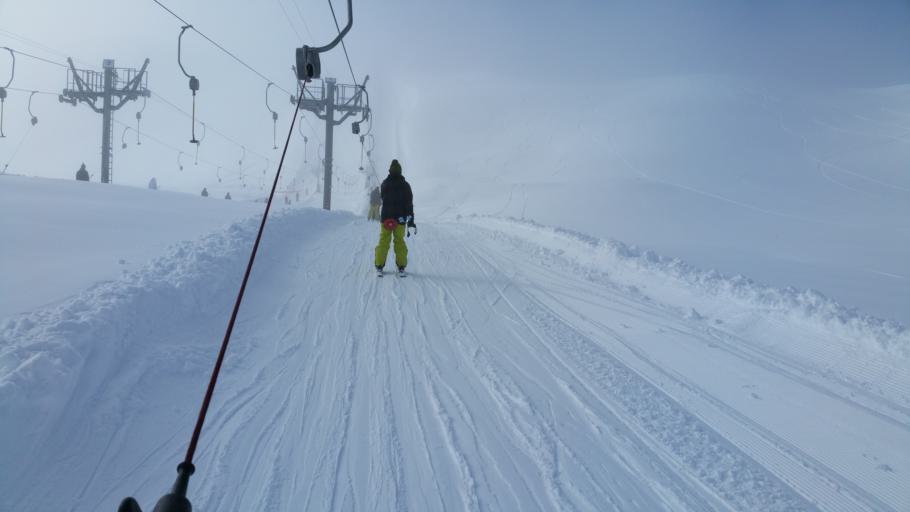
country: FR
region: Rhone-Alpes
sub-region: Departement de la Savoie
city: Saint-Etienne-de-Cuines
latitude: 45.2454
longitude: 6.2193
